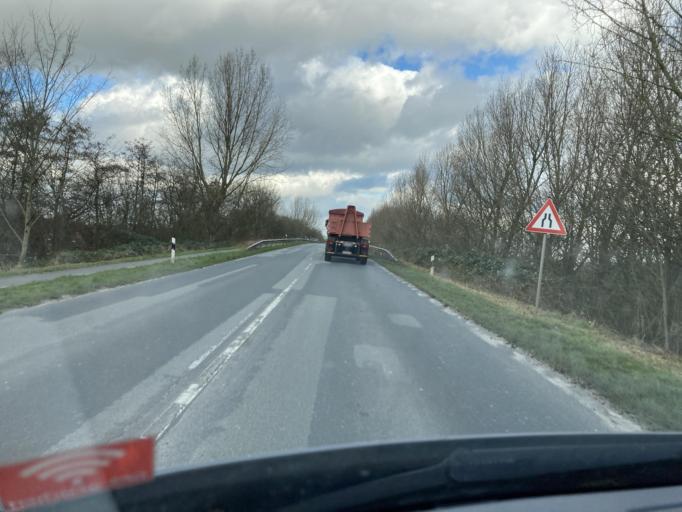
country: DE
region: Lower Saxony
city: Sande
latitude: 53.4995
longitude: 8.0243
